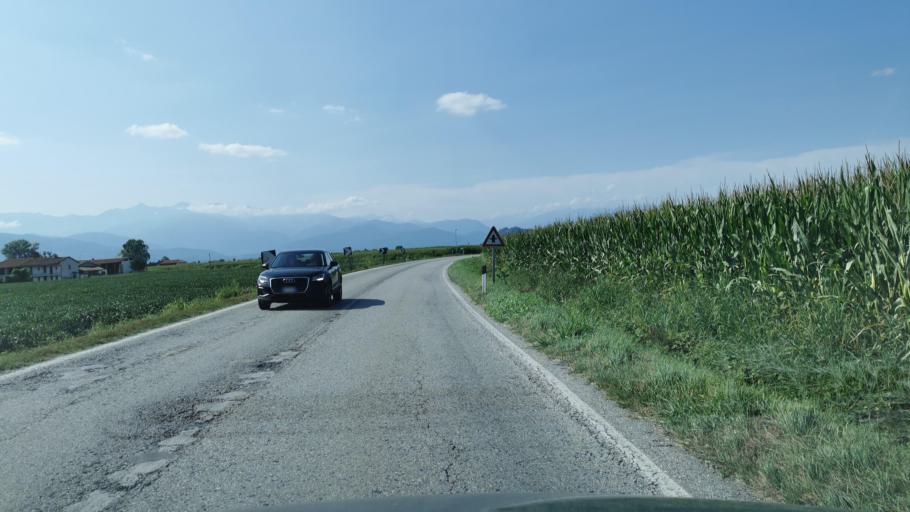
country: IT
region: Piedmont
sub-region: Provincia di Cuneo
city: Carde
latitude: 44.7379
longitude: 7.4171
